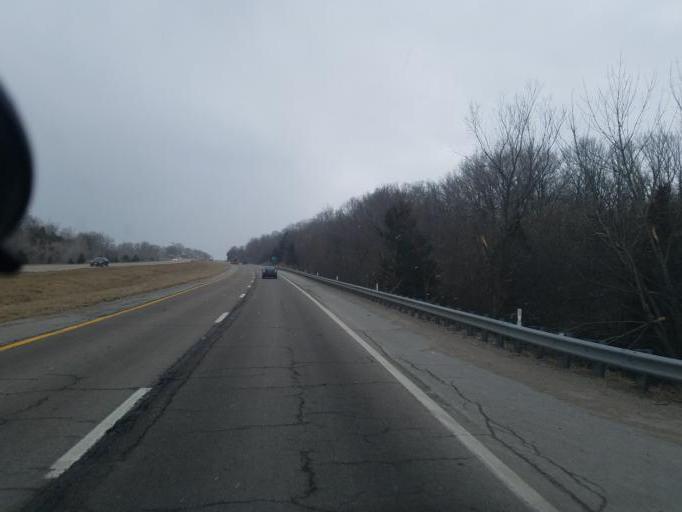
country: US
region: Missouri
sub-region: Boone County
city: Hallsville
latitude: 39.1240
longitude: -92.3326
